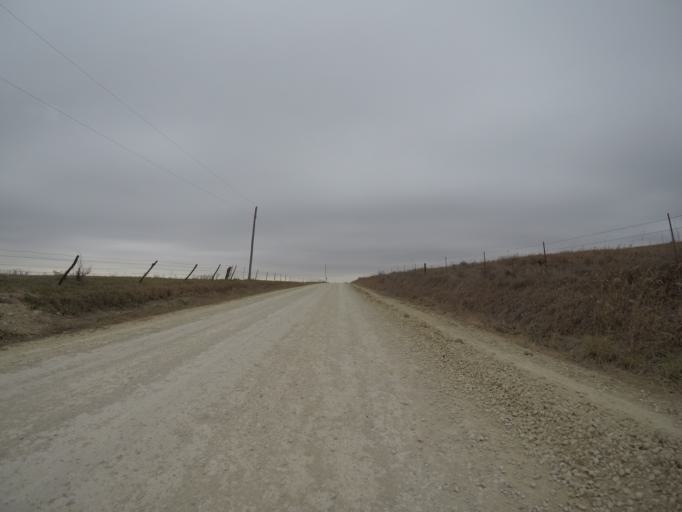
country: US
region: Kansas
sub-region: Wabaunsee County
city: Alma
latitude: 38.8536
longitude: -96.1133
